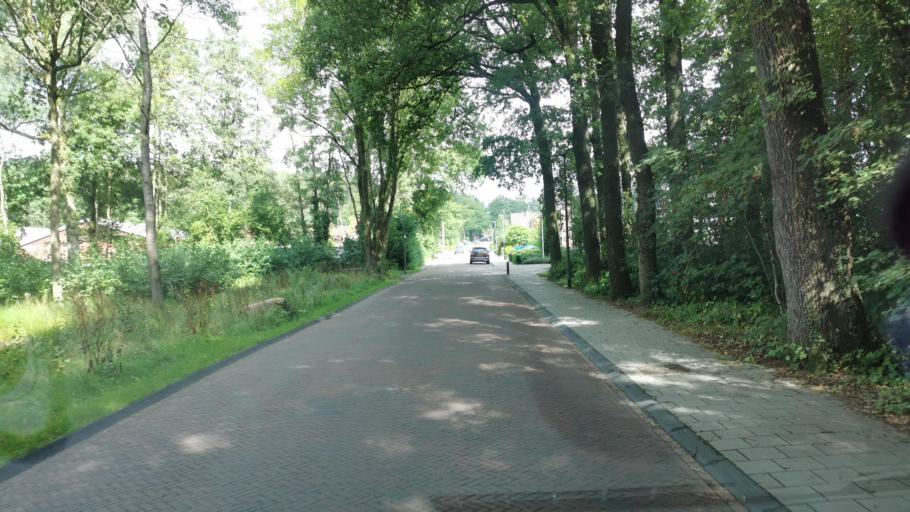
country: NL
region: Overijssel
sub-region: Gemeente Losser
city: Losser
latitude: 52.3113
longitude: 6.9891
